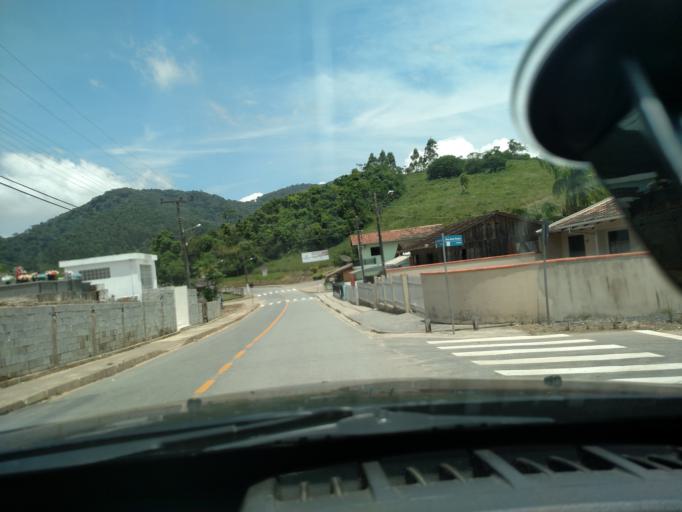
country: BR
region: Santa Catarina
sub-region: Gaspar
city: Gaspar
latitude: -26.9080
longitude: -48.8197
